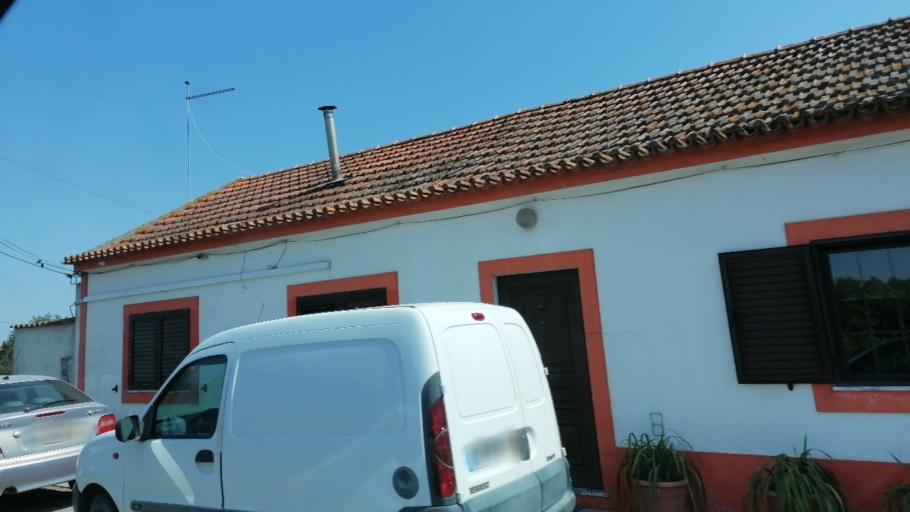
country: PT
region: Setubal
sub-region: Palmela
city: Palmela
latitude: 38.6144
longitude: -8.7604
